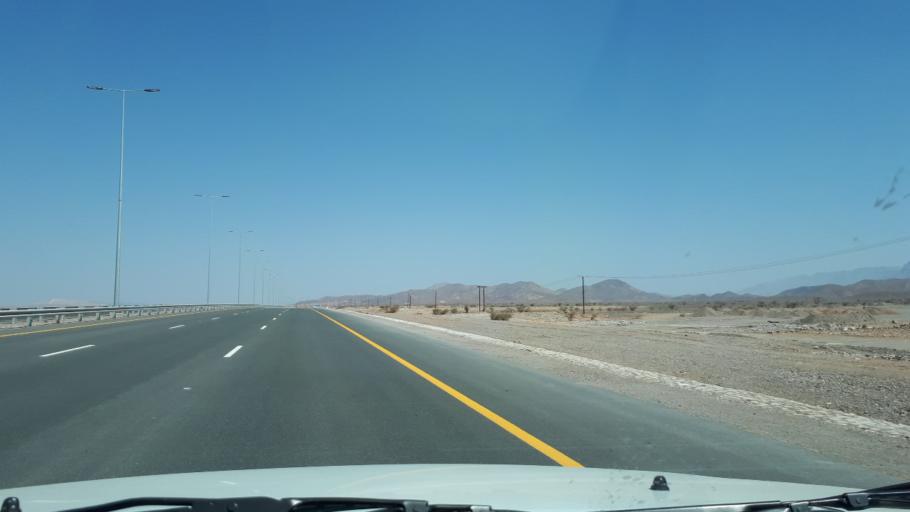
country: OM
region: Ash Sharqiyah
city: Badiyah
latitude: 22.4561
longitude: 59.0072
